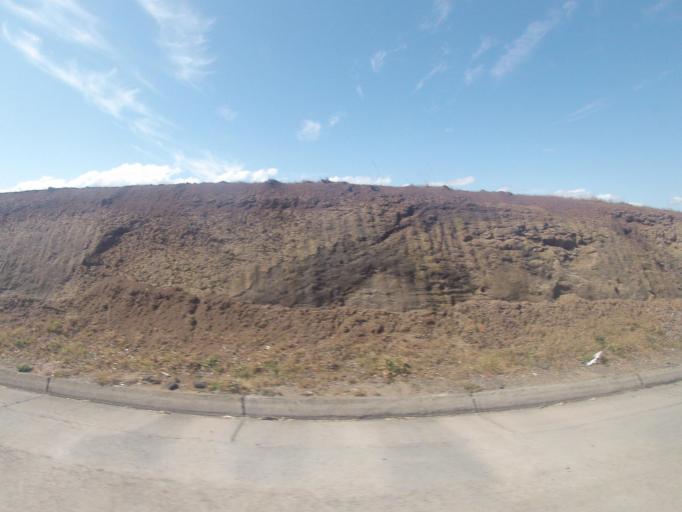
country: CL
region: Biobio
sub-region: Provincia de Biobio
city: Los Angeles
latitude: -37.4542
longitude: -72.4092
